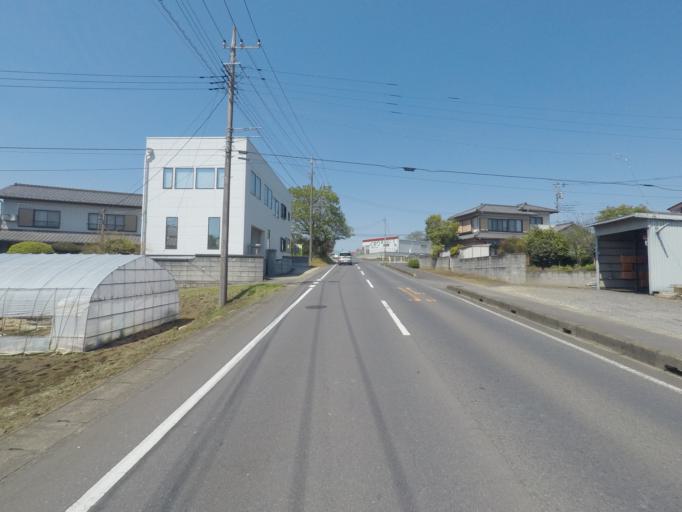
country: JP
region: Ibaraki
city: Ushiku
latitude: 35.9579
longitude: 140.1034
